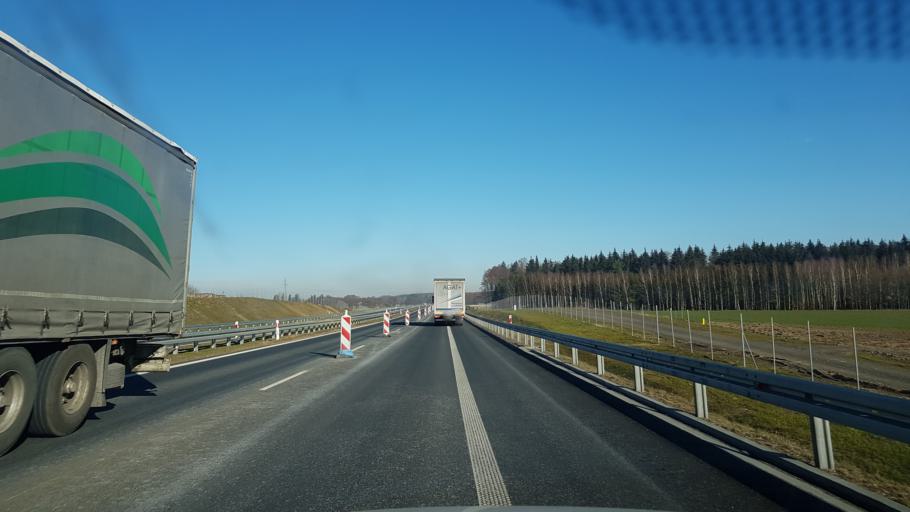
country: PL
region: West Pomeranian Voivodeship
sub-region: Powiat goleniowski
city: Przybiernow
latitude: 53.7971
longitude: 14.7767
